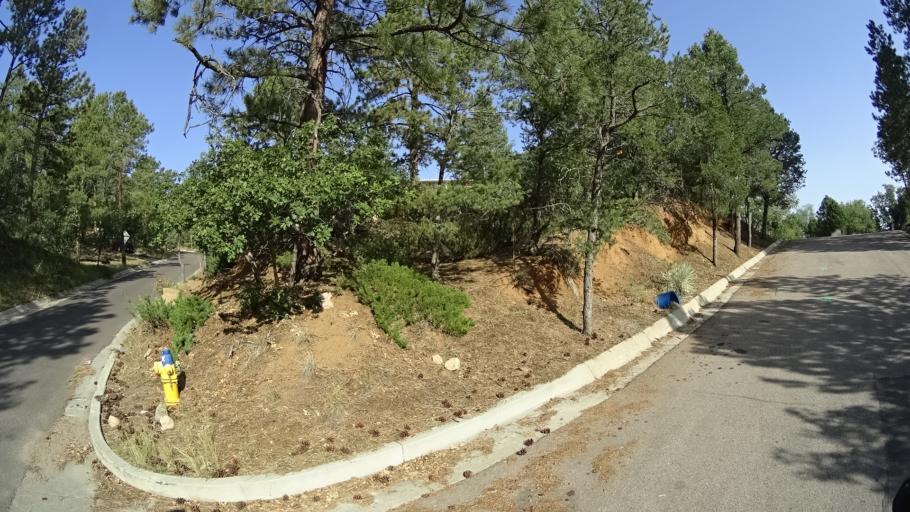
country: US
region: Colorado
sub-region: El Paso County
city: Colorado Springs
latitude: 38.8107
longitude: -104.8618
